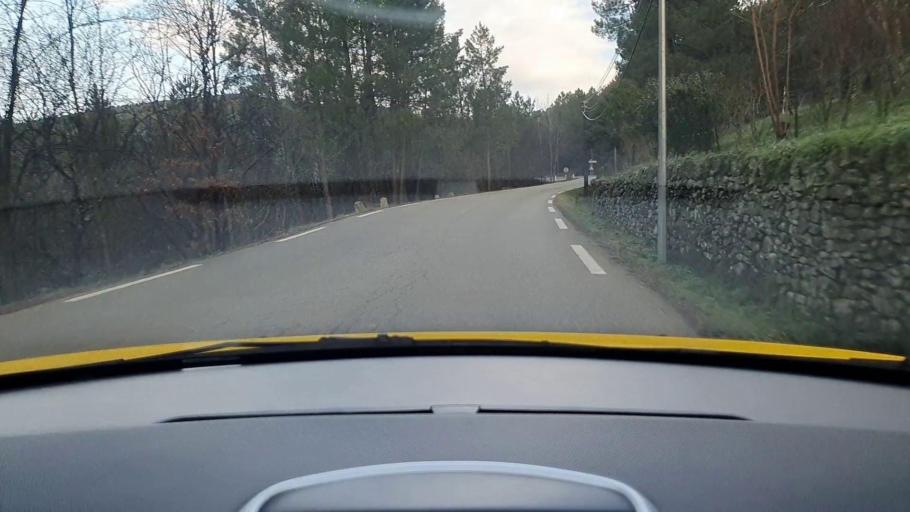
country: FR
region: Languedoc-Roussillon
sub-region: Departement du Gard
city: Les Salles-du-Gardon
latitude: 44.2525
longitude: 4.0447
